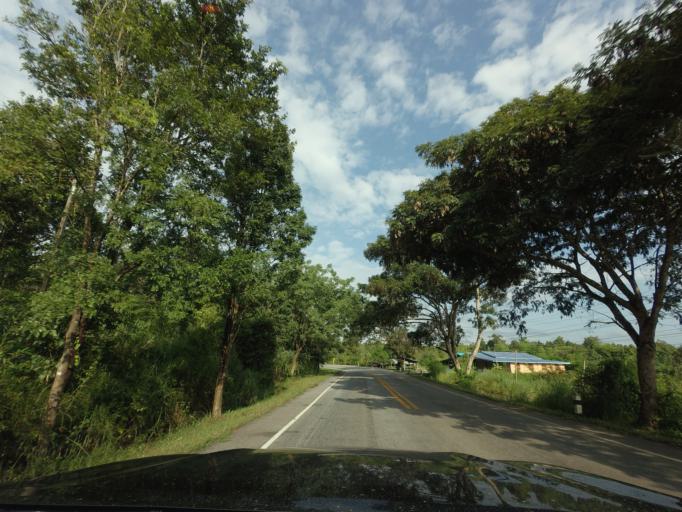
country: TH
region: Nong Khai
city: Pho Tak
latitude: 17.8071
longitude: 102.3336
